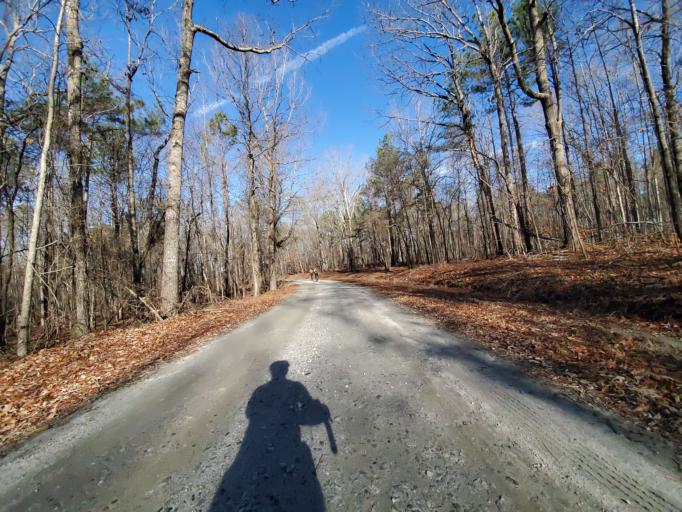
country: US
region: Georgia
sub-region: Fulton County
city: Chattahoochee Hills
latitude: 33.5600
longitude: -84.8051
